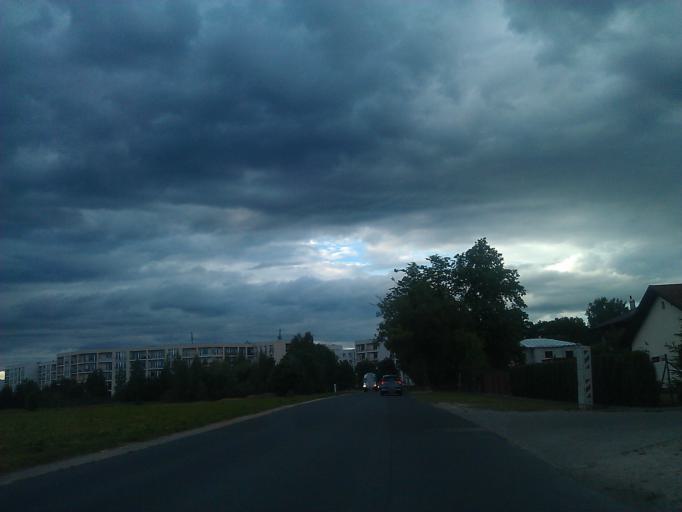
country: LV
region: Stopini
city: Ulbroka
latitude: 56.9531
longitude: 24.2441
